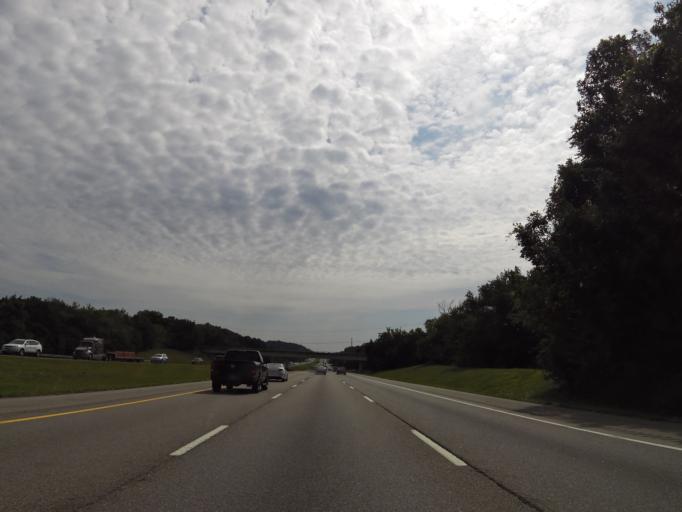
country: US
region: Tennessee
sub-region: Knox County
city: Mascot
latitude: 35.9966
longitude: -83.7129
